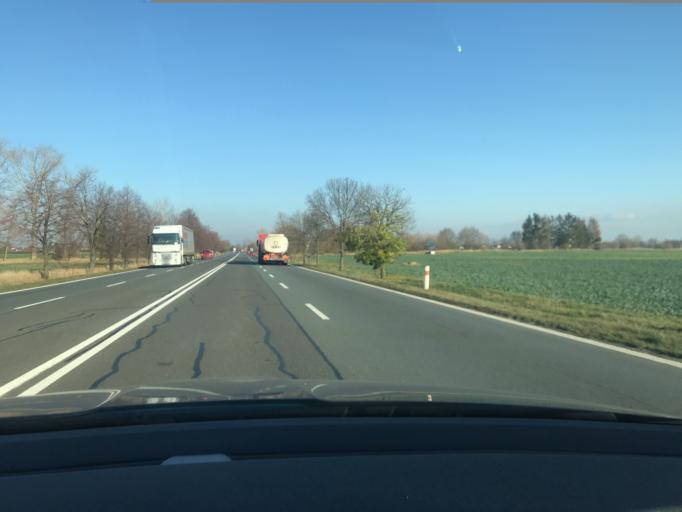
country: CZ
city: Stezery
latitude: 50.2125
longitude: 15.7840
